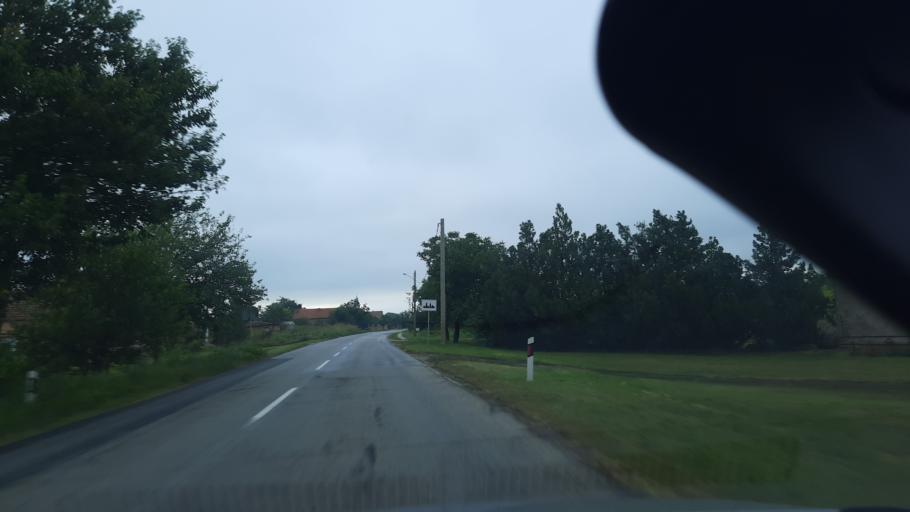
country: RS
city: Farkazdin
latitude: 45.1913
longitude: 20.4662
